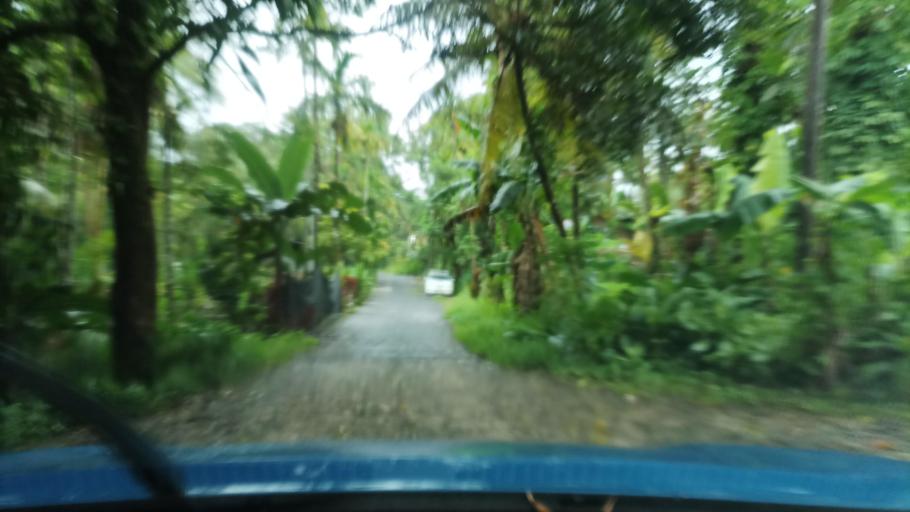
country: FM
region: Pohnpei
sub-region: Kolonia Municipality
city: Kolonia
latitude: 6.9599
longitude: 158.2136
